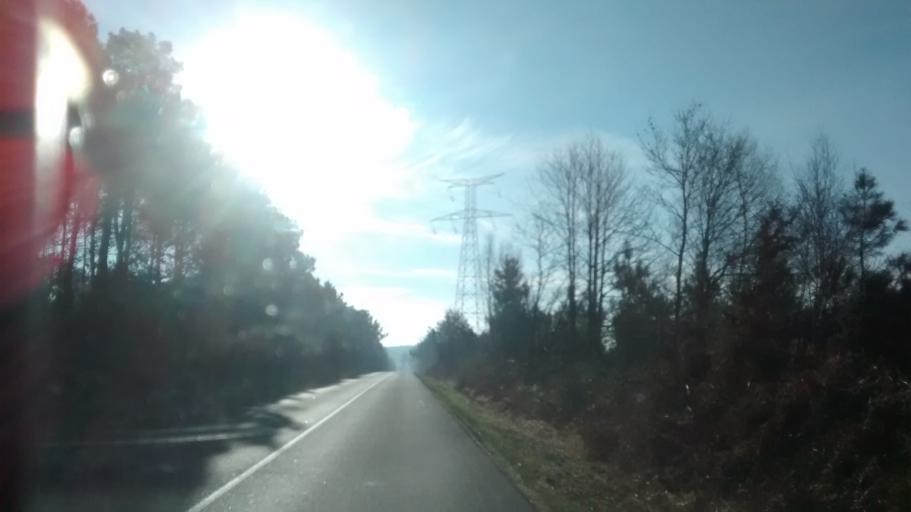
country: FR
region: Brittany
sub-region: Departement d'Ille-et-Vilaine
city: La Bouexiere
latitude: 48.1519
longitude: -1.4078
